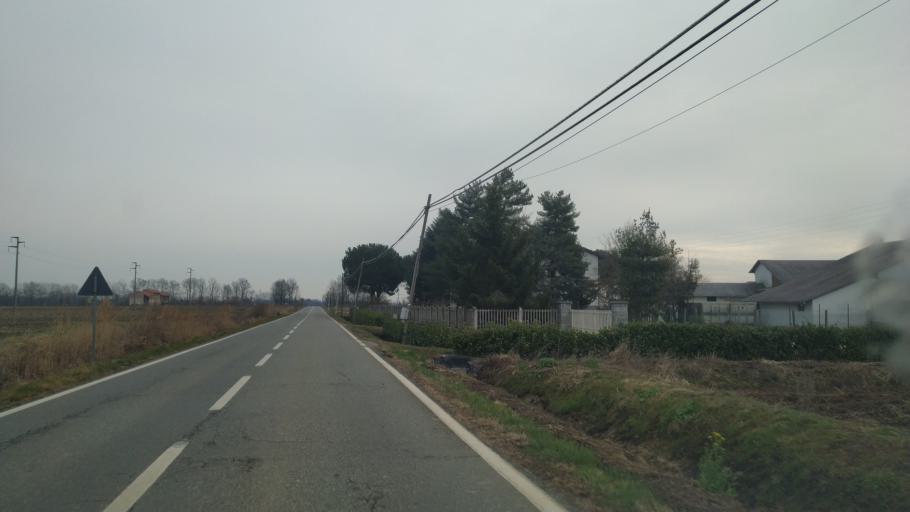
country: IT
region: Piedmont
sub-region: Provincia di Vercelli
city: San Giacomo Vercellese
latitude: 45.4935
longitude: 8.3035
